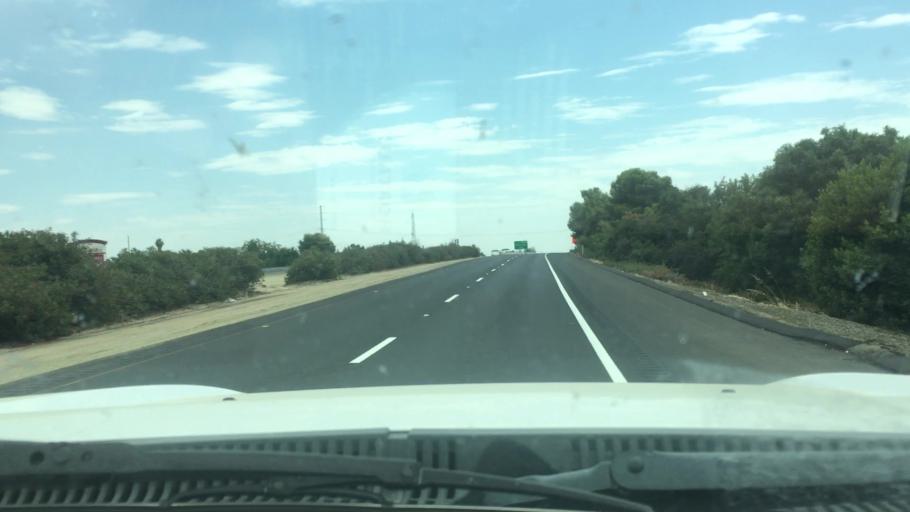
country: US
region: California
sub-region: Tulare County
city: Porterville
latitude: 36.0834
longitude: -119.0394
